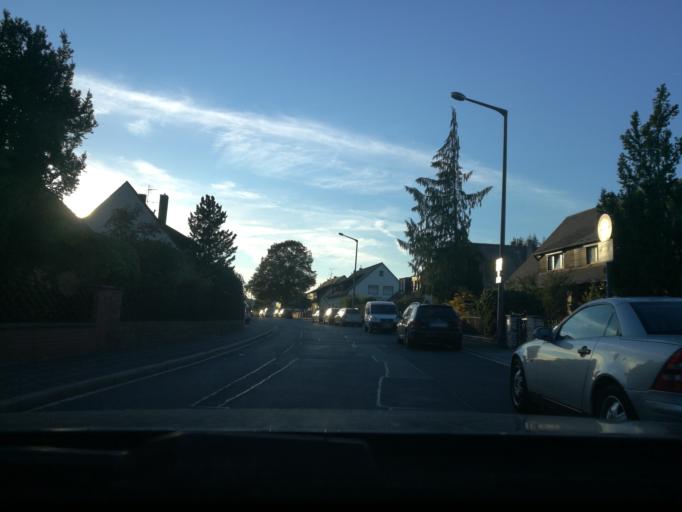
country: DE
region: Bavaria
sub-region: Regierungsbezirk Mittelfranken
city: Furth
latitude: 49.5058
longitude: 10.9506
